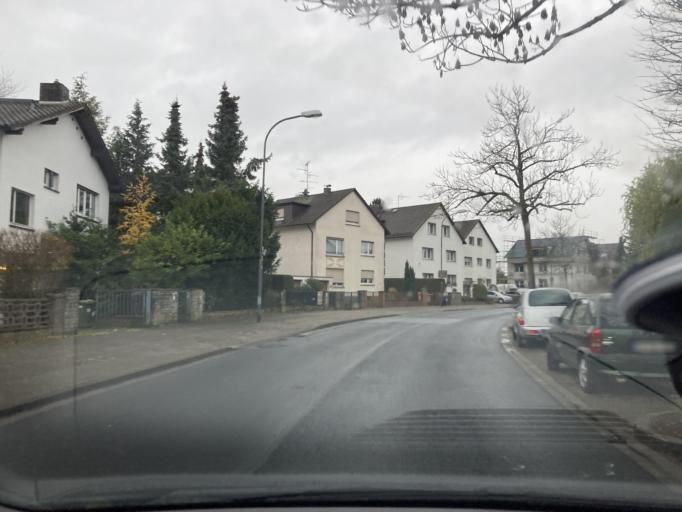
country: DE
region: Hesse
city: Heusenstamm
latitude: 50.0842
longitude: 8.8096
